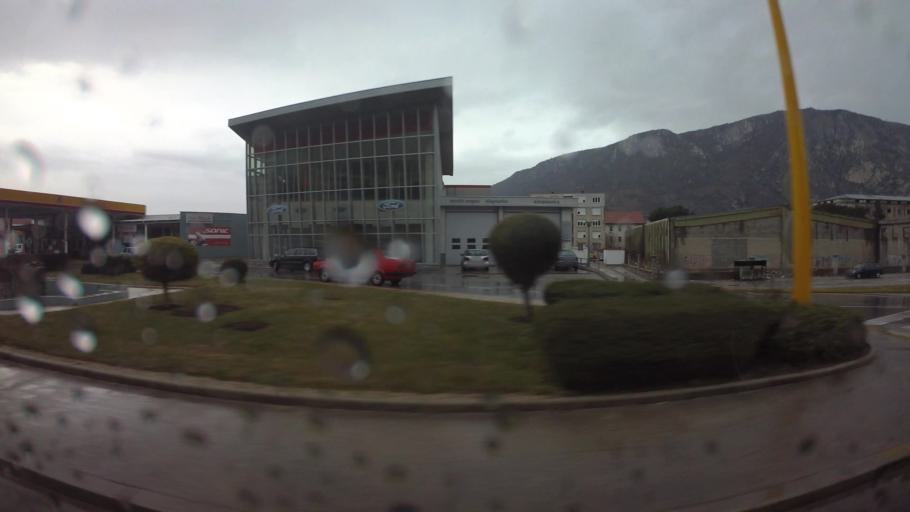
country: BA
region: Federation of Bosnia and Herzegovina
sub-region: Hercegovacko-Bosanski Kanton
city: Mostar
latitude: 43.3269
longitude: 17.8252
